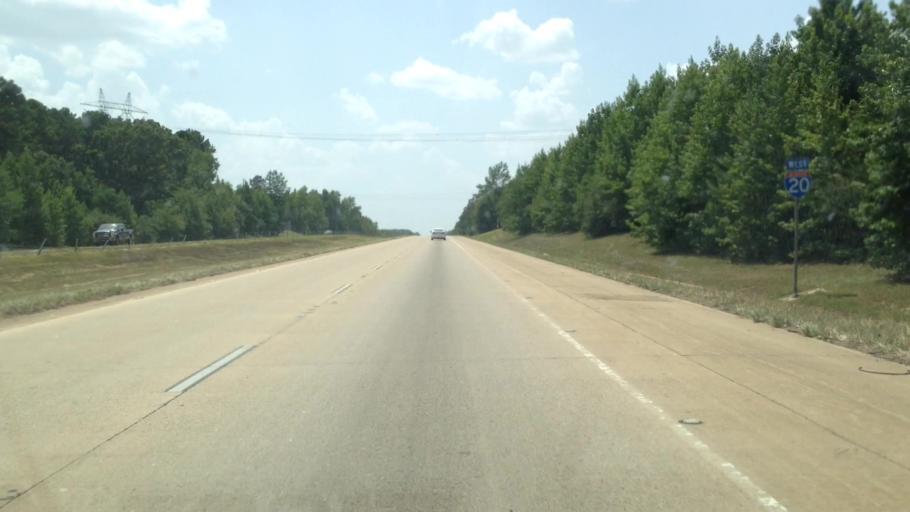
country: US
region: Louisiana
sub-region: Lincoln Parish
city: Grambling
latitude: 32.5425
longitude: -92.7213
